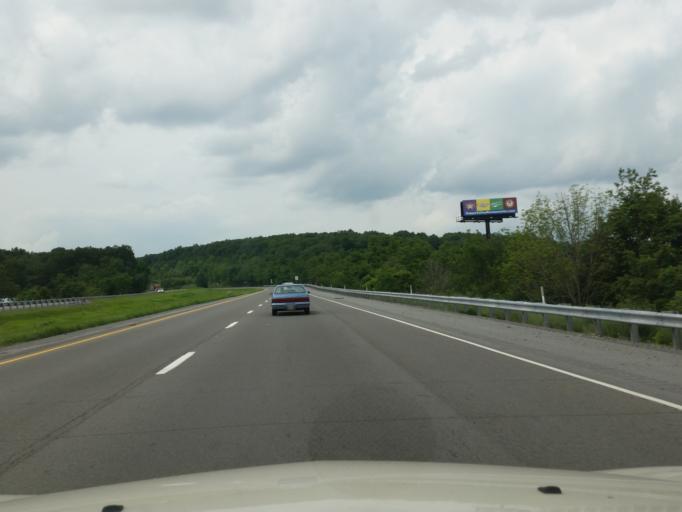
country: US
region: Pennsylvania
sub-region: Juniata County
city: Mifflintown
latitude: 40.5871
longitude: -77.3739
